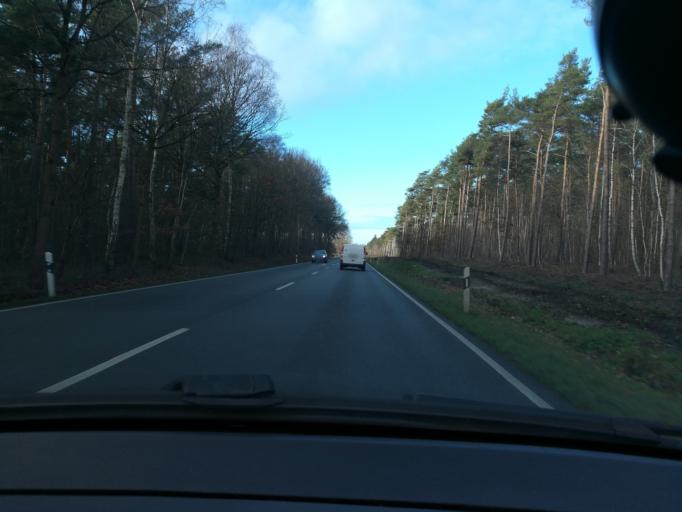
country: DE
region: Lower Saxony
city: Uchte
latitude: 52.5371
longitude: 8.8732
